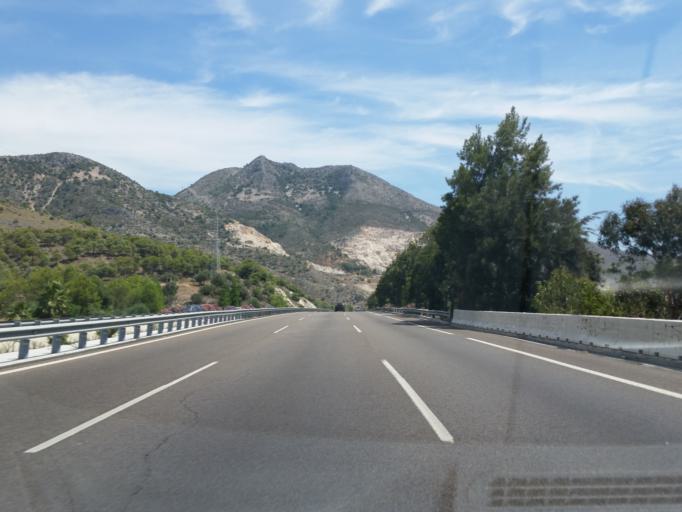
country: ES
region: Andalusia
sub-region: Provincia de Malaga
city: Benalmadena
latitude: 36.5976
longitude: -4.5748
